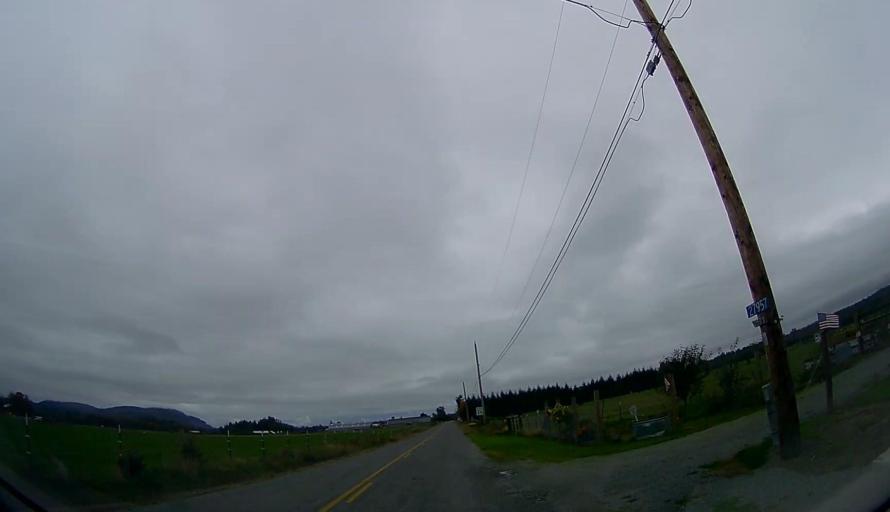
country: US
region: Washington
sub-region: Skagit County
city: Sedro-Woolley
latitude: 48.5148
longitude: -122.1410
